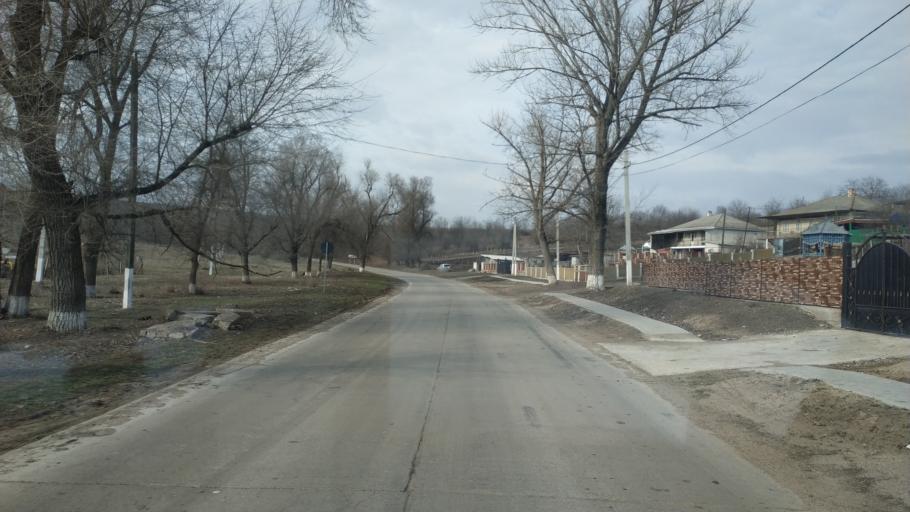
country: MD
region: Chisinau
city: Vadul lui Voda
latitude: 47.0077
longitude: 29.1186
